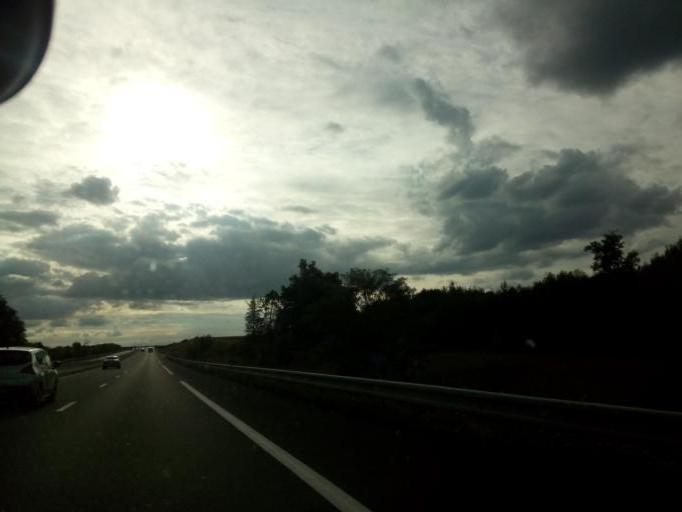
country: FR
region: Centre
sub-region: Departement du Loir-et-Cher
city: Saint-Georges-sur-Cher
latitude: 47.2949
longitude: 1.1436
